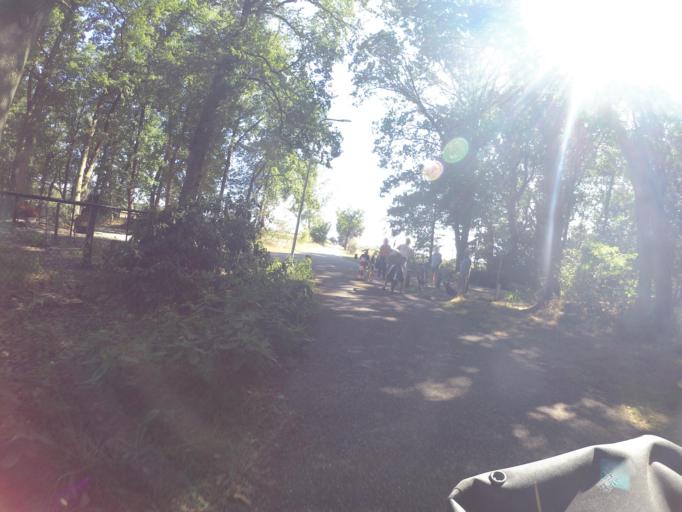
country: NL
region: Overijssel
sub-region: Gemeente Twenterand
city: Den Ham
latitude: 52.4003
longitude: 6.4333
